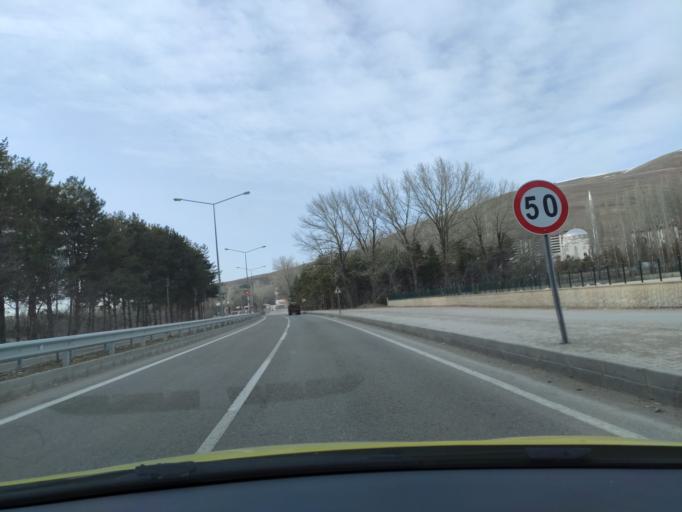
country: TR
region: Bayburt
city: Bayburt
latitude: 40.2368
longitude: 40.2528
